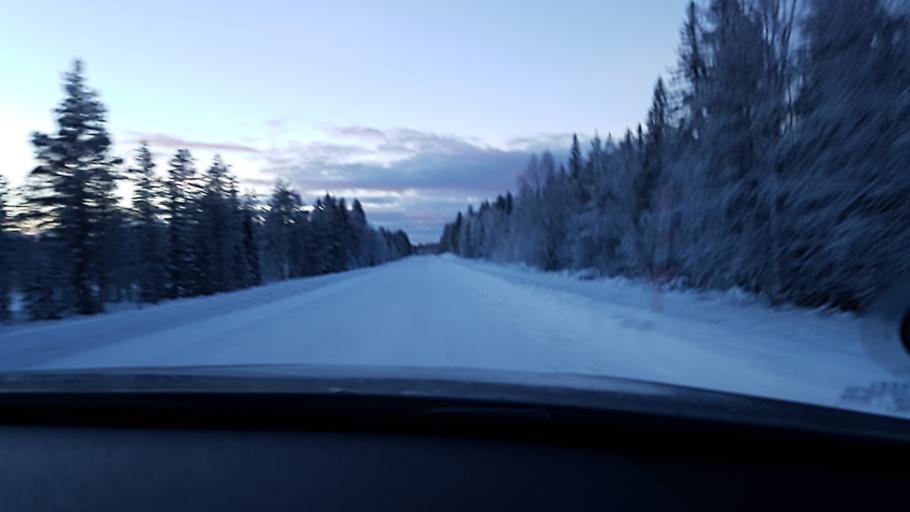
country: SE
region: Vaesterbotten
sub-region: Storumans Kommun
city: Storuman
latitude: 65.1016
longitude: 17.1756
